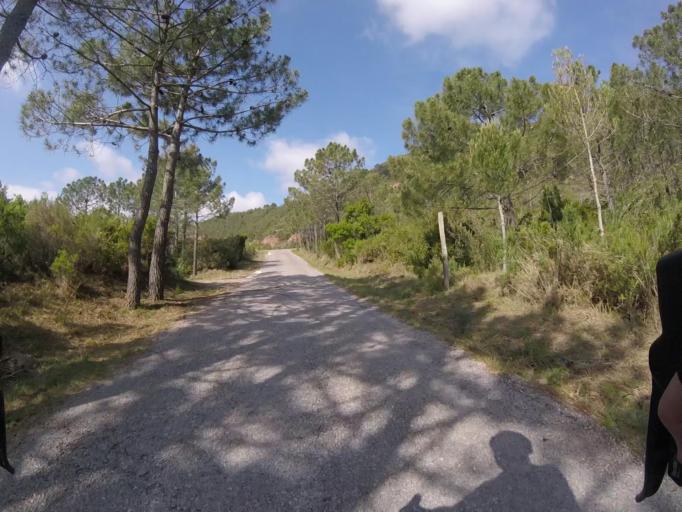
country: ES
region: Valencia
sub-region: Provincia de Castello
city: Benicassim
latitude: 40.0782
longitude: 0.0273
